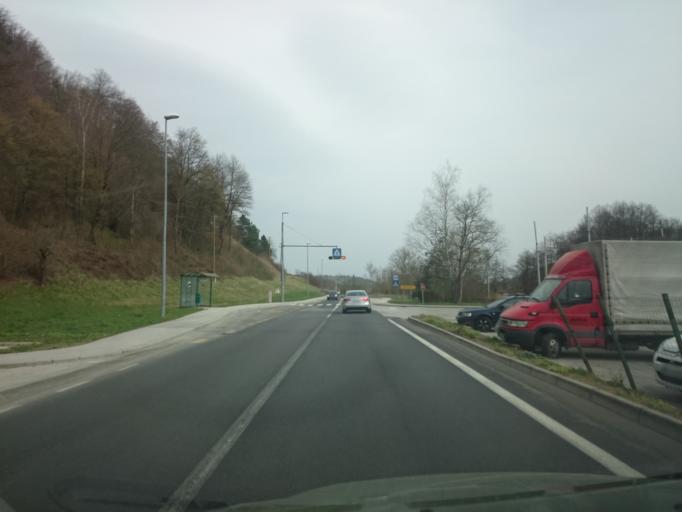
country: SI
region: Store
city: Store
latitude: 46.2194
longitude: 15.3366
